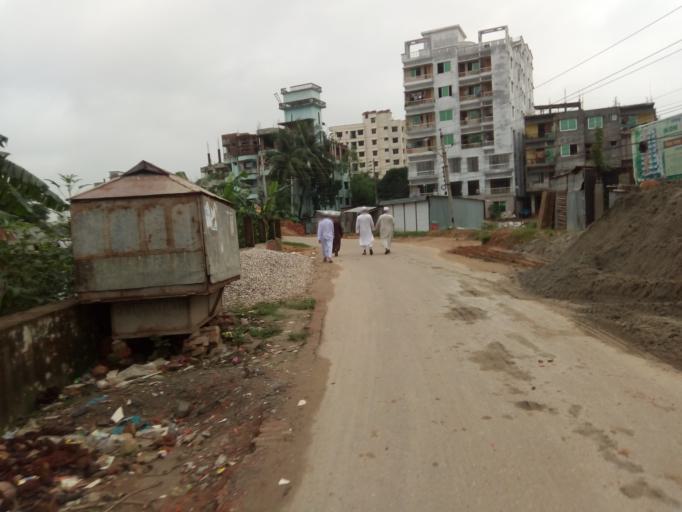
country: BD
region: Dhaka
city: Tungi
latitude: 23.8465
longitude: 90.4196
